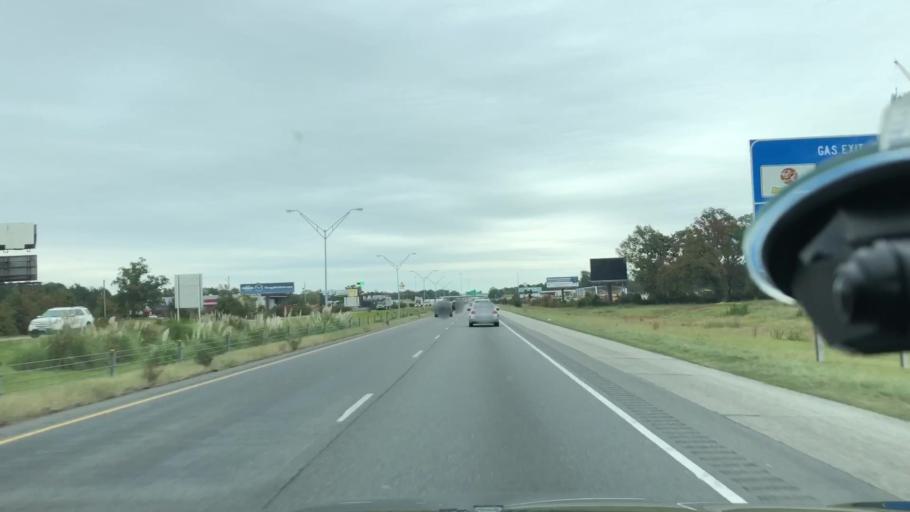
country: US
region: Arkansas
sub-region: Miller County
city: Texarkana
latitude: 33.4735
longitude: -94.0187
